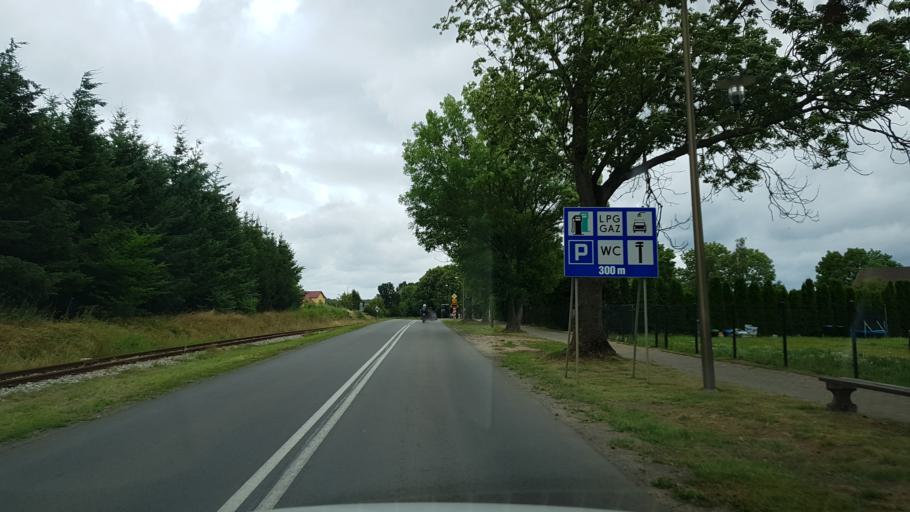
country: PL
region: West Pomeranian Voivodeship
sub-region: Powiat gryficki
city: Rewal
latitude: 54.0740
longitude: 15.0342
